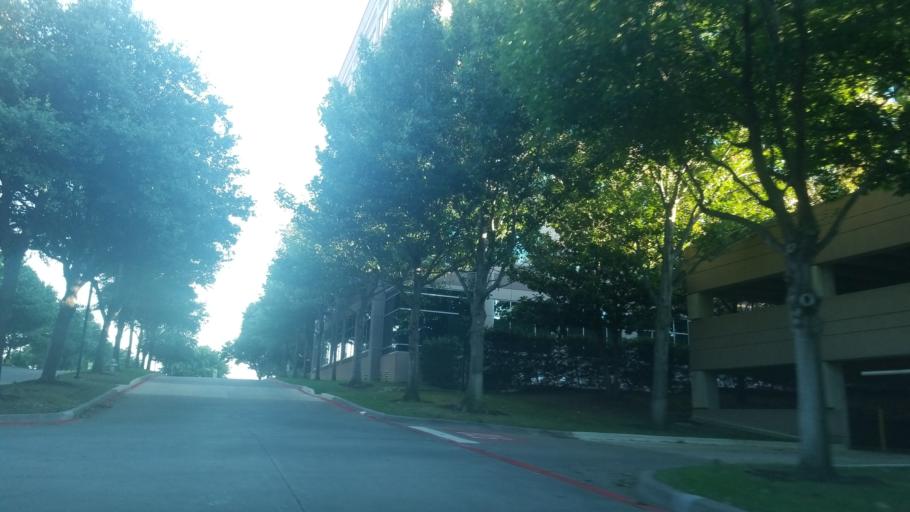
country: US
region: Texas
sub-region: Dallas County
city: Irving
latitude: 32.8787
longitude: -96.9600
